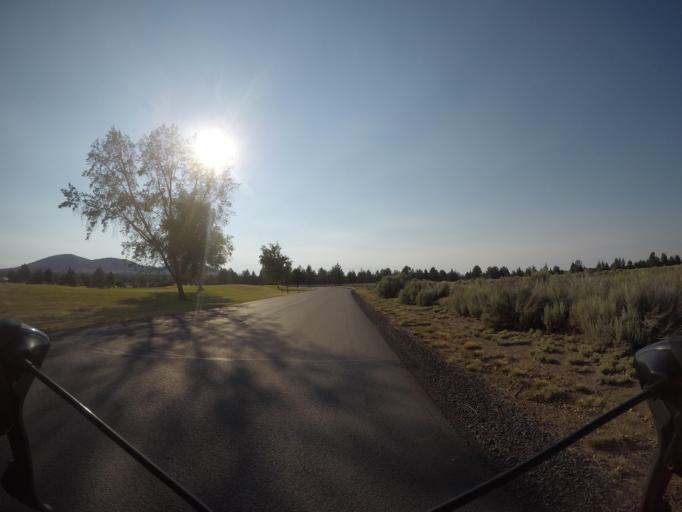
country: US
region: Oregon
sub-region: Deschutes County
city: Redmond
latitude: 44.2628
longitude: -121.2543
